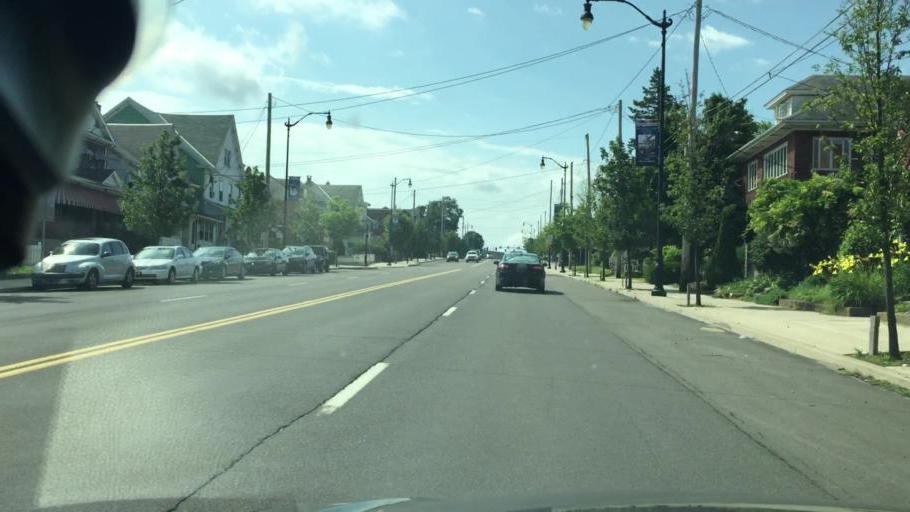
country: US
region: Pennsylvania
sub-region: Luzerne County
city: West Hazleton
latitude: 40.9634
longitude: -75.9969
